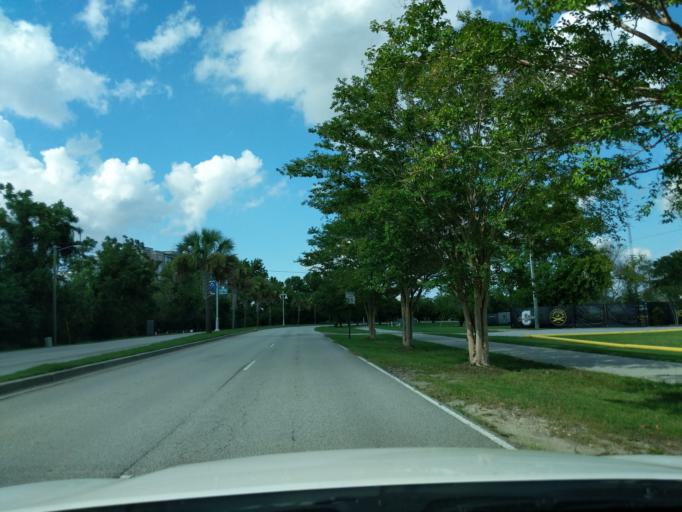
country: US
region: South Carolina
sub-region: Charleston County
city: Charleston
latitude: 32.7950
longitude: -79.9044
